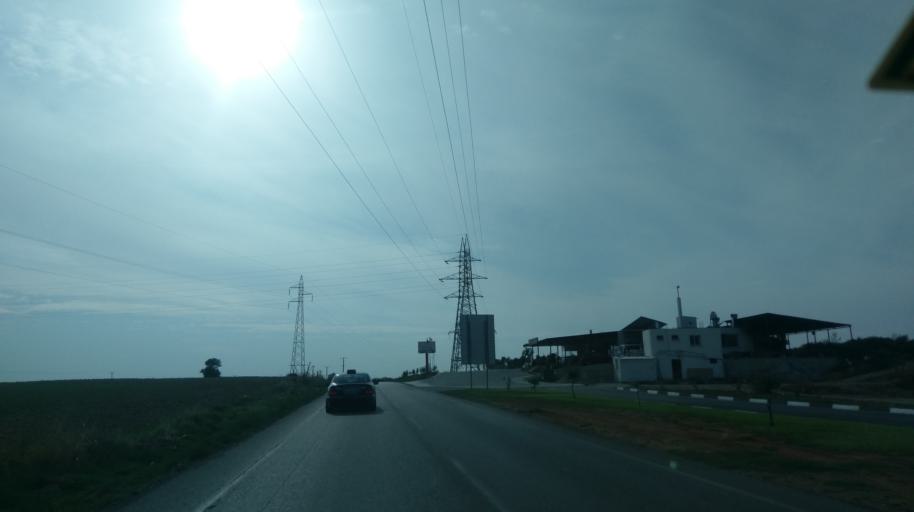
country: CY
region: Ammochostos
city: Leonarisso
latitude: 35.3815
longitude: 34.0406
